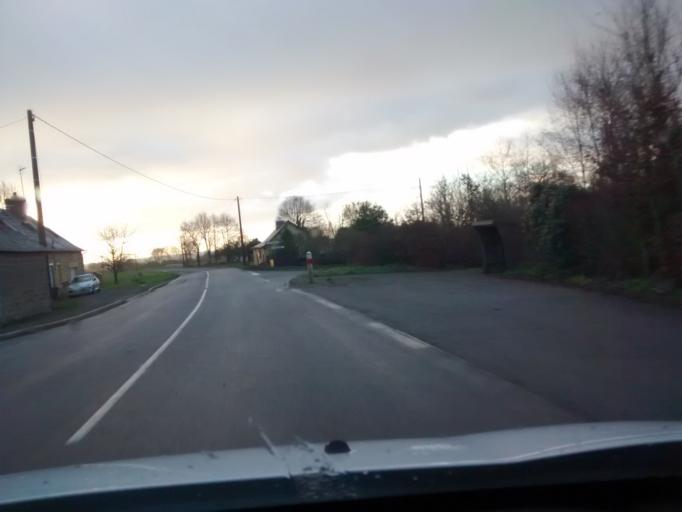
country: FR
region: Brittany
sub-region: Departement d'Ille-et-Vilaine
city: Bais
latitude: 47.9868
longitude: -1.2855
